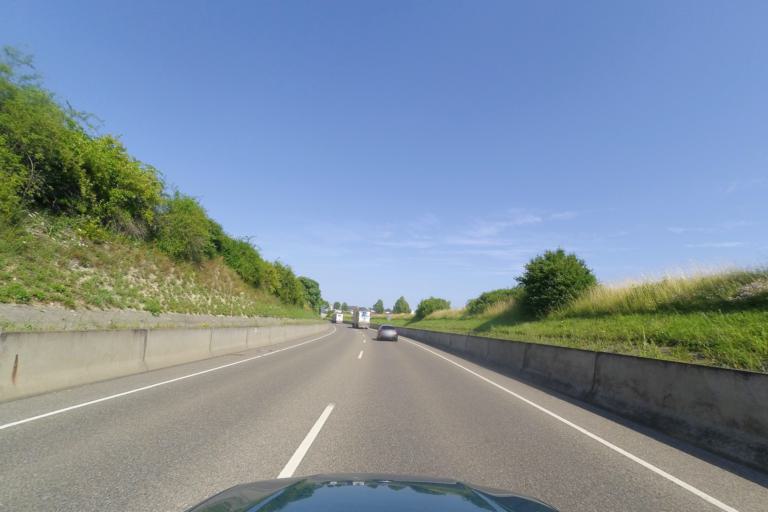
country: DE
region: Baden-Wuerttemberg
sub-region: Regierungsbezirk Stuttgart
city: Herbrechtingen
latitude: 48.6283
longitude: 10.1696
